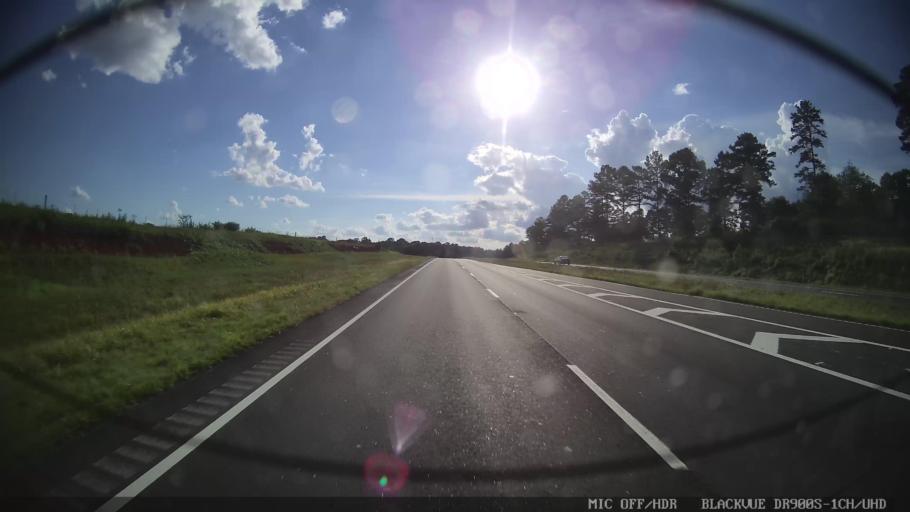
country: US
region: Georgia
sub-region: Floyd County
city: Lindale
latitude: 34.2066
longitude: -85.0802
